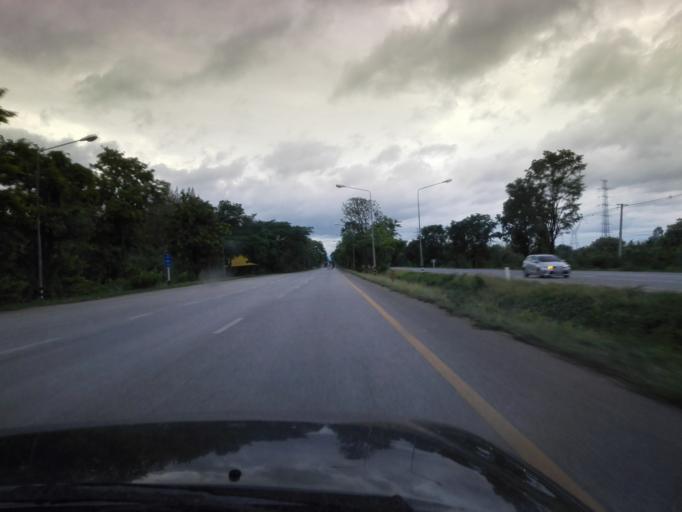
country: TH
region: Tak
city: Tak
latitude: 16.8043
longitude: 99.1456
